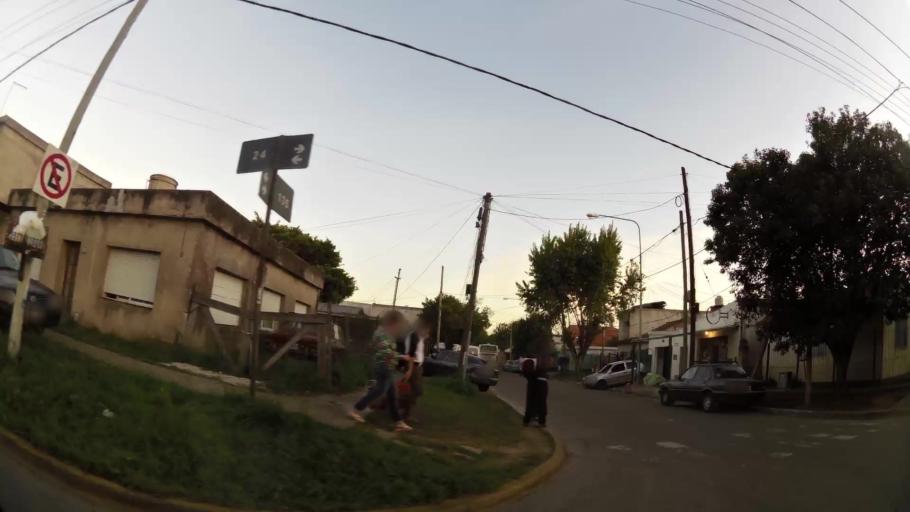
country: AR
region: Buenos Aires
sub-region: Partido de Quilmes
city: Quilmes
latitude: -34.7789
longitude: -58.2150
